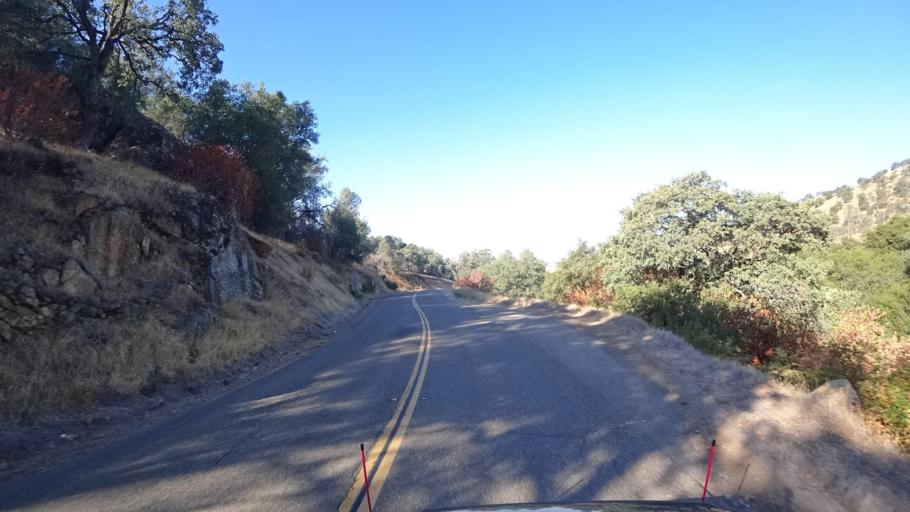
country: US
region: California
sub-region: Mariposa County
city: Mariposa
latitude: 37.5591
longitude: -120.1685
